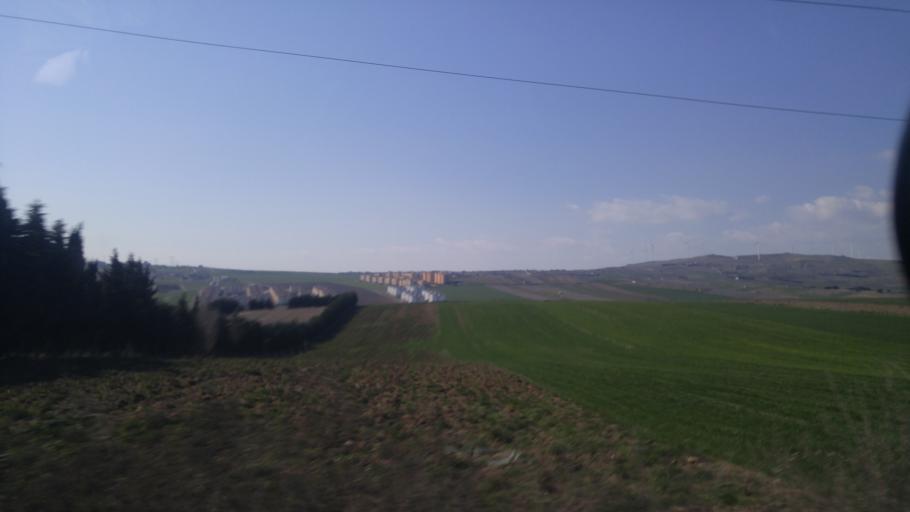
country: TR
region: Istanbul
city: Canta
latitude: 41.0922
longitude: 28.1093
